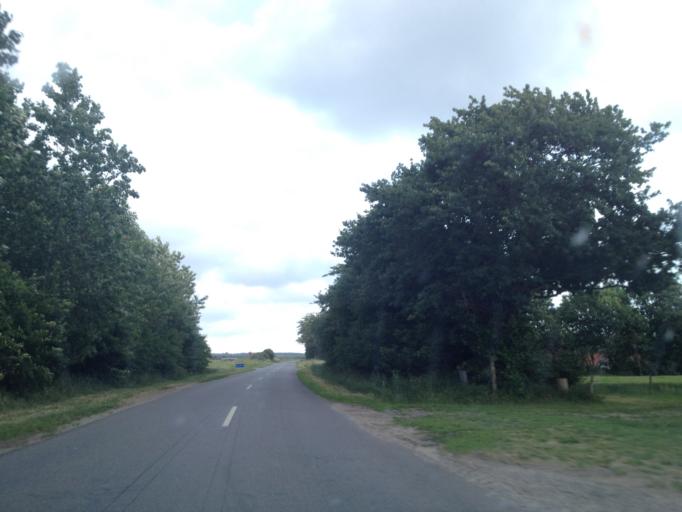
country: DK
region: South Denmark
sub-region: Tonder Kommune
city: Sherrebek
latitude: 55.1735
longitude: 8.7232
